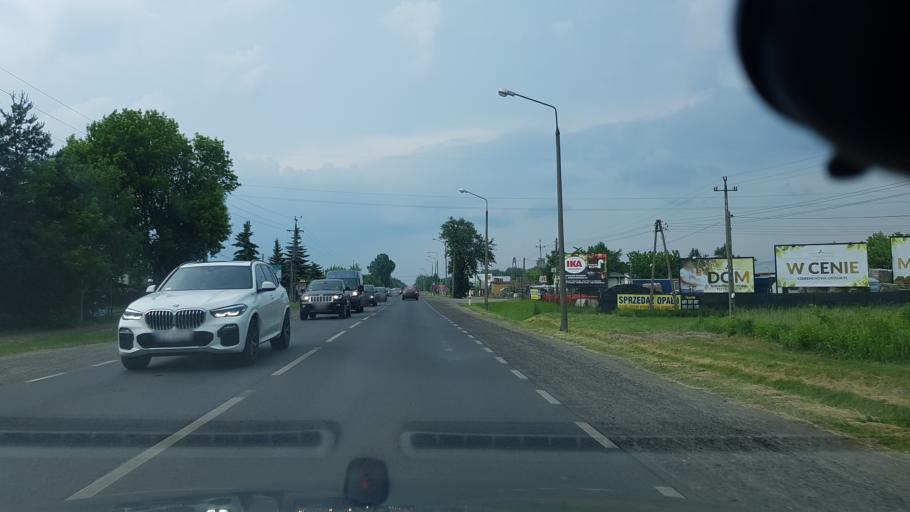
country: PL
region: Masovian Voivodeship
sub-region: Powiat legionowski
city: Michalow-Reginow
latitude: 52.4187
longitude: 20.9682
